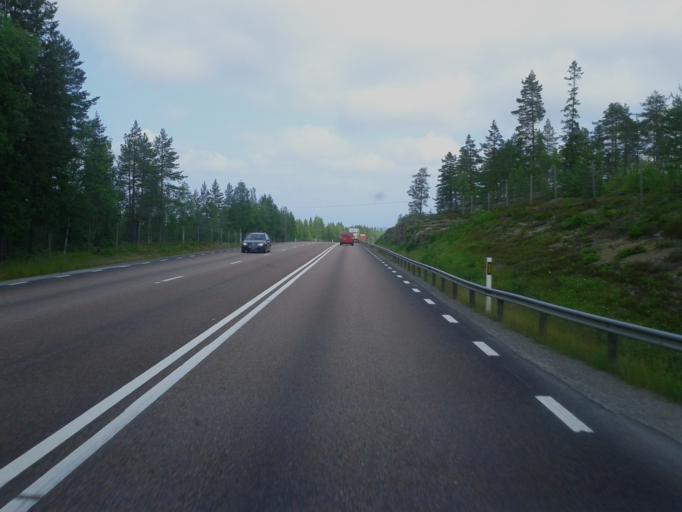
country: SE
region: Vaesterbotten
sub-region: Skelleftea Kommun
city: Burea
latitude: 64.4433
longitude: 21.2832
